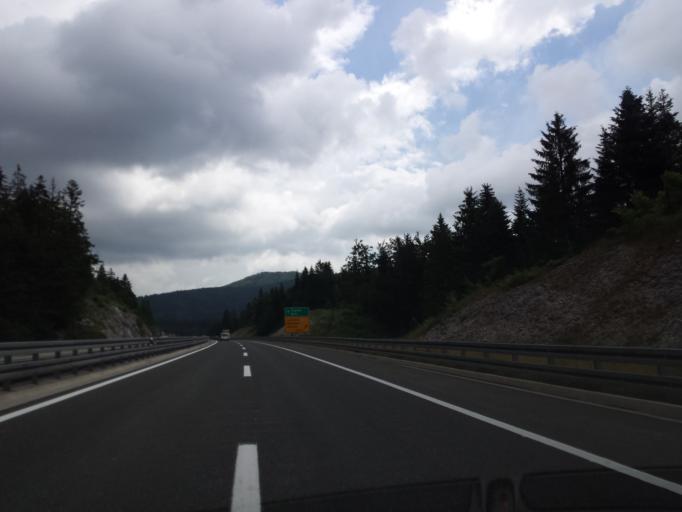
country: HR
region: Primorsko-Goranska
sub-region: Grad Delnice
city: Delnice
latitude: 45.3711
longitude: 14.7847
